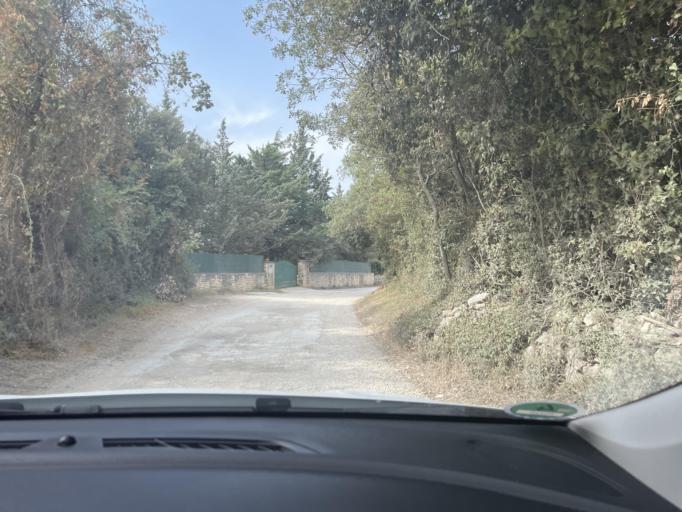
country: HR
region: Istarska
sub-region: Grad Rovinj
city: Rovinj
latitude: 45.0427
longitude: 13.7118
